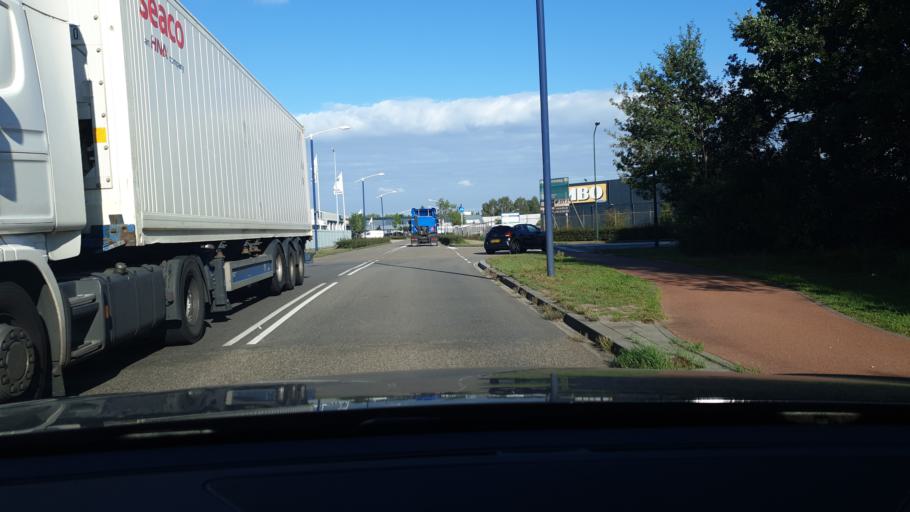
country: NL
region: North Brabant
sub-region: Gemeente Veghel
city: Eerde
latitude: 51.6126
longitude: 5.5109
